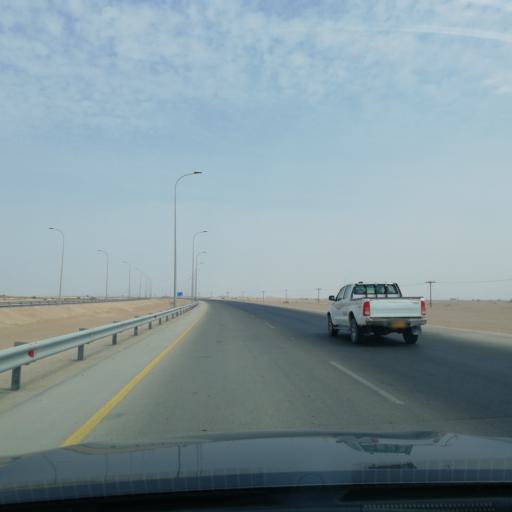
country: OM
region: Zufar
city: Salalah
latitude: 17.6906
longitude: 54.0521
